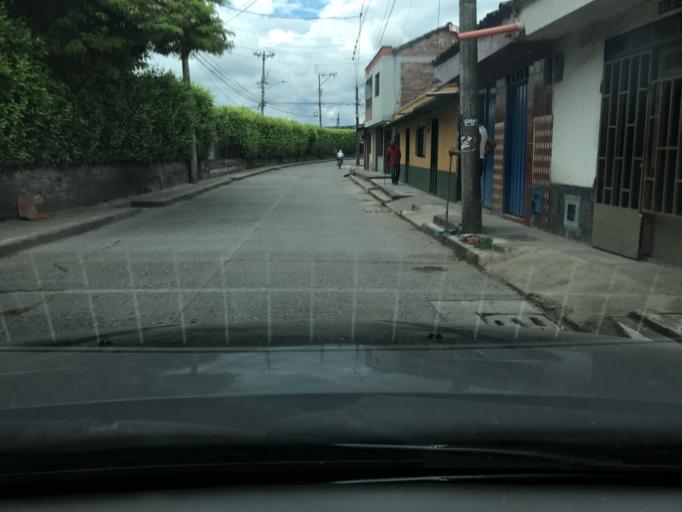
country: CO
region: Valle del Cauca
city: Cartago
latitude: 4.7591
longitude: -75.9320
